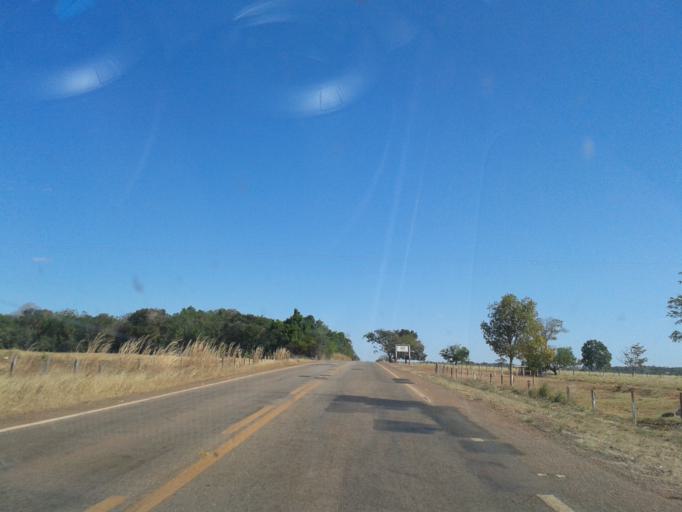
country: BR
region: Goias
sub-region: Crixas
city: Crixas
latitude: -14.1696
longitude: -50.3696
